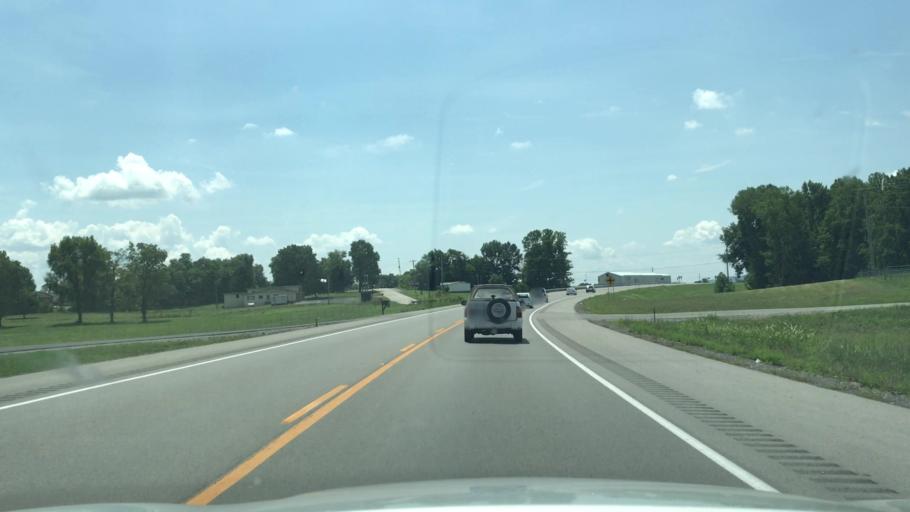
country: US
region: Tennessee
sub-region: Pickett County
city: Byrdstown
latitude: 36.6256
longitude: -85.0893
